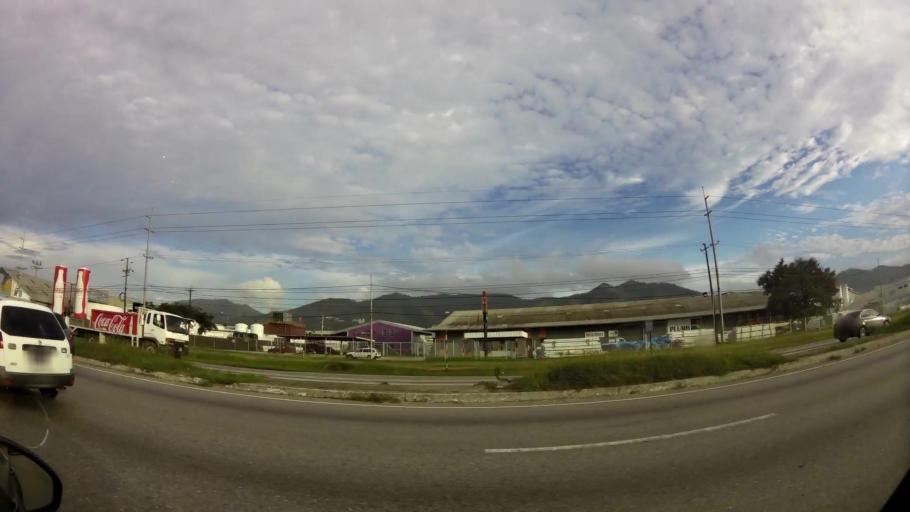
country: TT
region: Tunapuna/Piarco
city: Tunapuna
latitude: 10.6381
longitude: -61.3853
